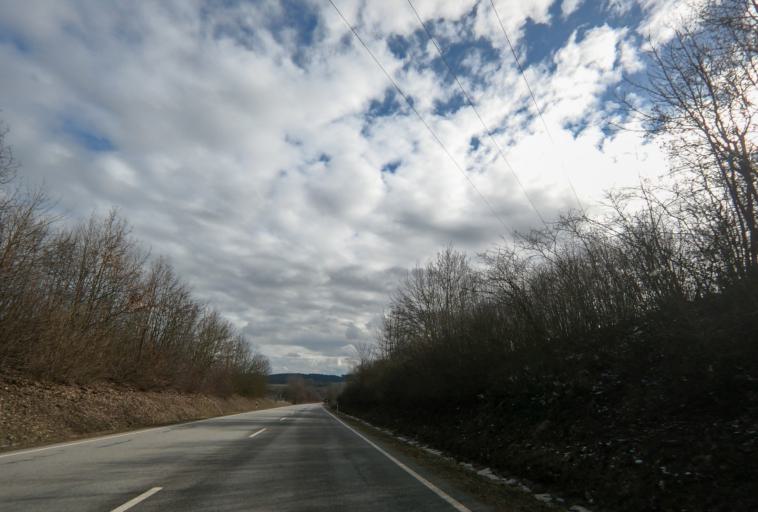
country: DE
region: Bavaria
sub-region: Lower Bavaria
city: Mallersdorf-Pfaffenberg
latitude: 48.7618
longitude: 12.1975
